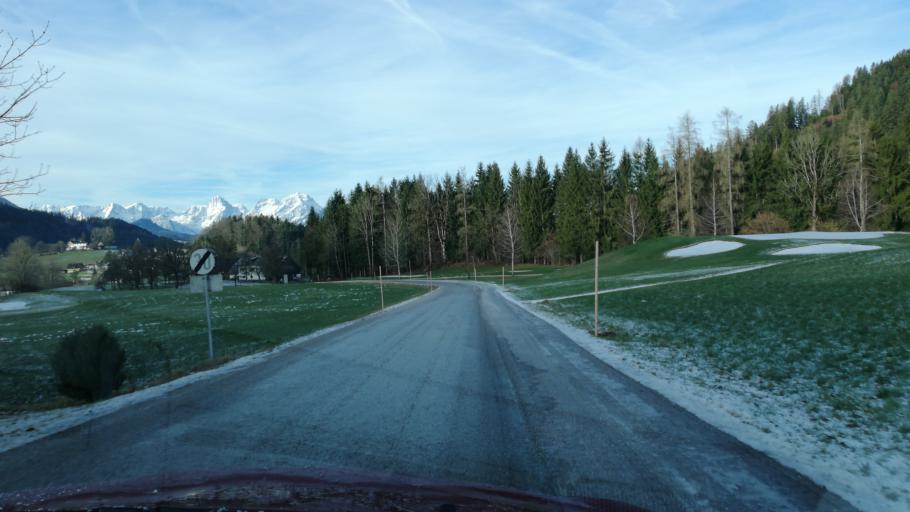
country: AT
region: Upper Austria
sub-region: Politischer Bezirk Kirchdorf an der Krems
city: Rossleithen
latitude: 47.7165
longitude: 14.3571
